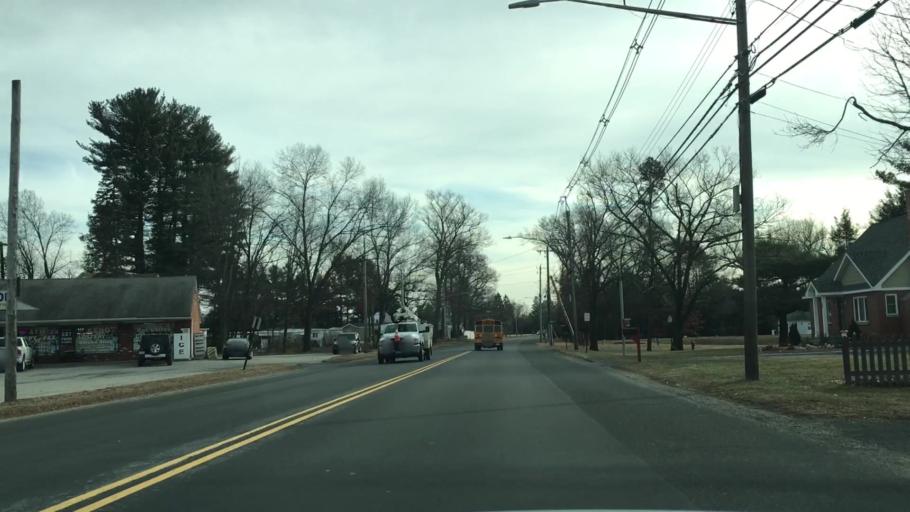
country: US
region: Massachusetts
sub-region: Hampden County
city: Westfield
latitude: 42.0987
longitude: -72.7634
